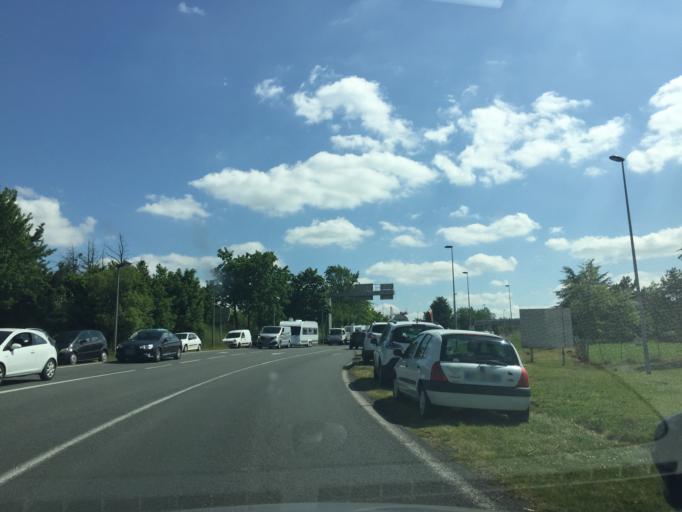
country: FR
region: Aquitaine
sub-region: Departement du Lot-et-Garonne
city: Boe
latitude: 44.1668
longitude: 0.6065
